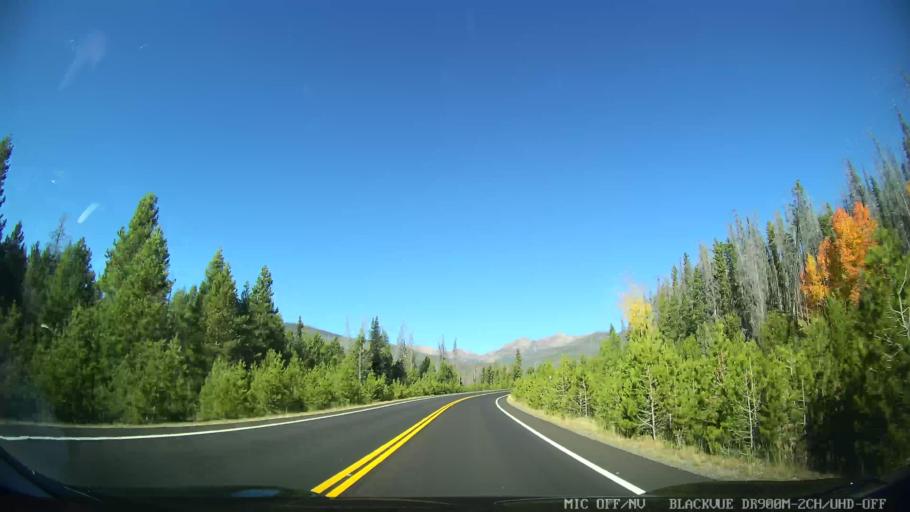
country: US
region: Colorado
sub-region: Grand County
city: Granby
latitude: 40.3200
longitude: -105.8499
